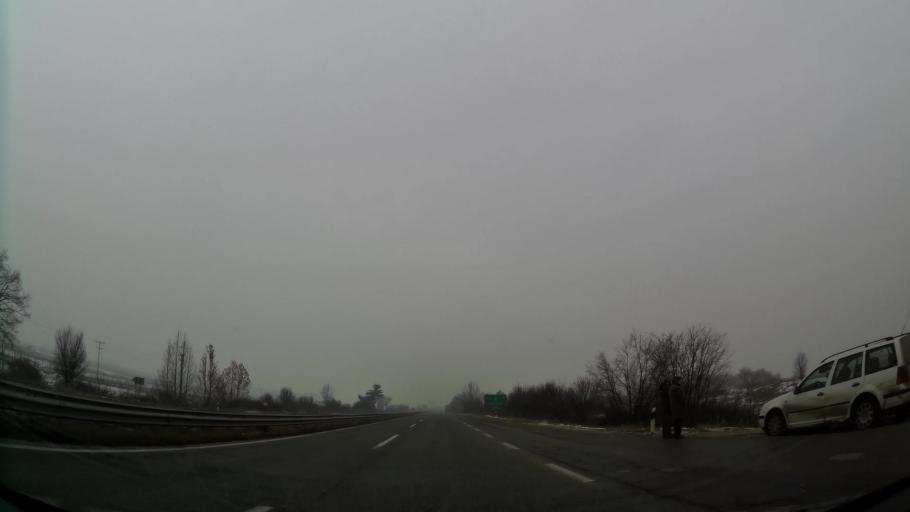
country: MK
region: Petrovec
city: Petrovec
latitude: 41.9524
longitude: 21.6307
